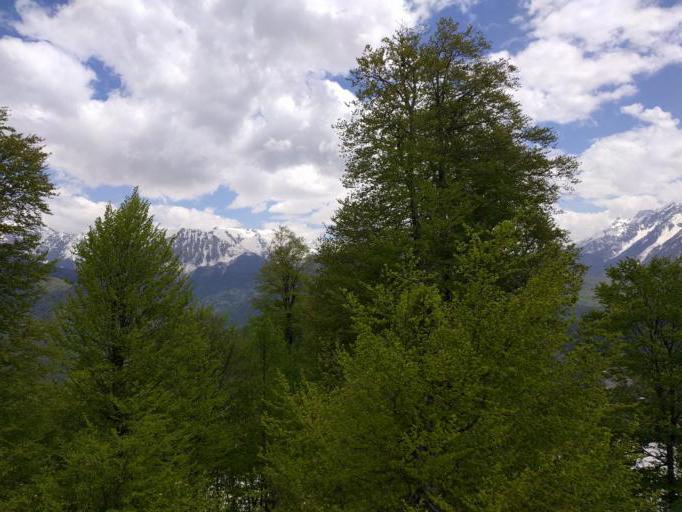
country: RU
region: Krasnodarskiy
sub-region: Sochi City
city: Krasnaya Polyana
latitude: 43.6556
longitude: 40.3186
